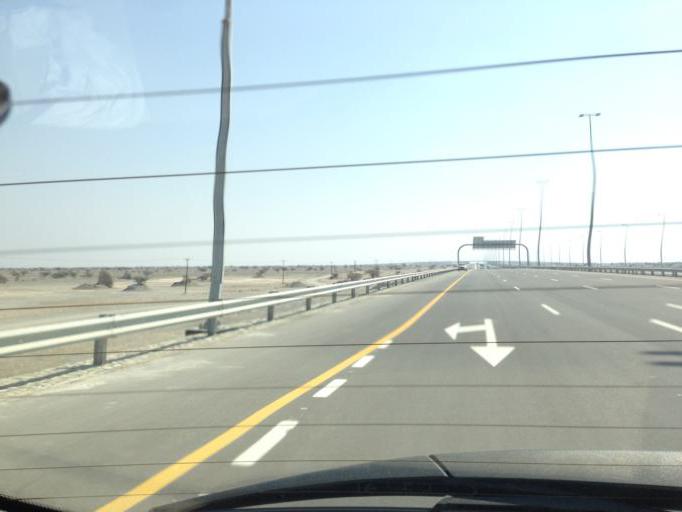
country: OM
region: Al Batinah
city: Barka'
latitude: 23.5757
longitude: 57.7516
